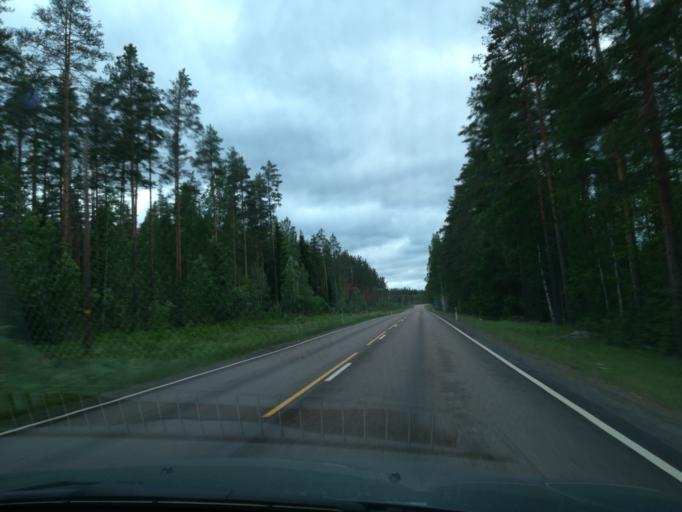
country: FI
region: Southern Savonia
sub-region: Mikkeli
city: Ristiina
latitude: 61.3413
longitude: 27.3734
